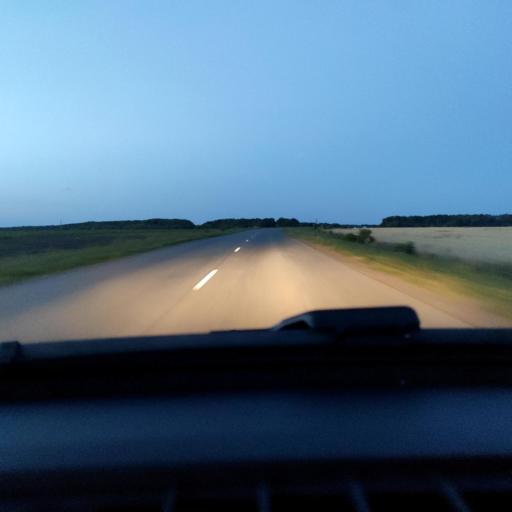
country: RU
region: Lipetsk
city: Zadonsk
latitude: 52.2977
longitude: 38.7909
